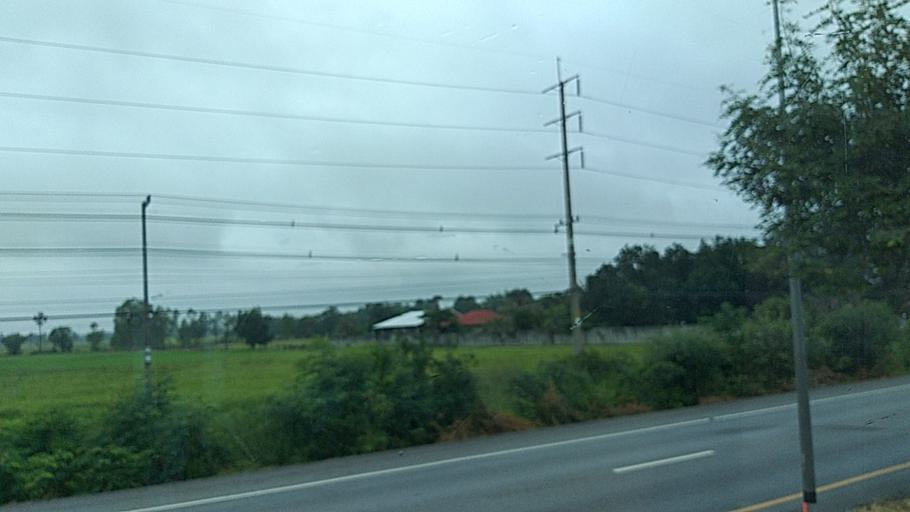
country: TH
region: Nakhon Ratchasima
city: Phimai
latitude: 15.2775
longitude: 102.4184
